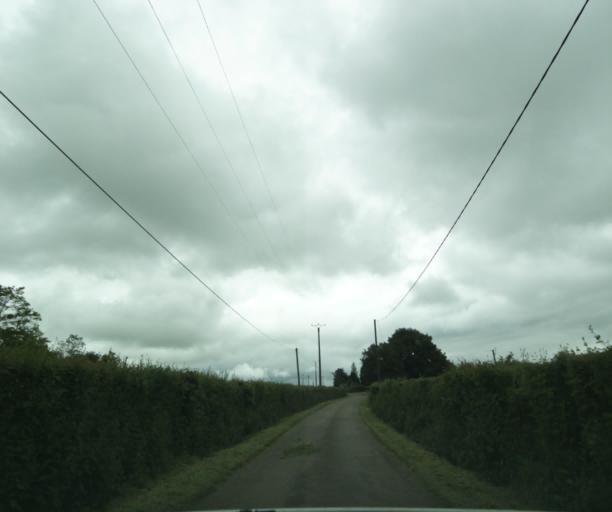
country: FR
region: Bourgogne
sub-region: Departement de Saone-et-Loire
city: Charolles
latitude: 46.4512
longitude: 4.2847
